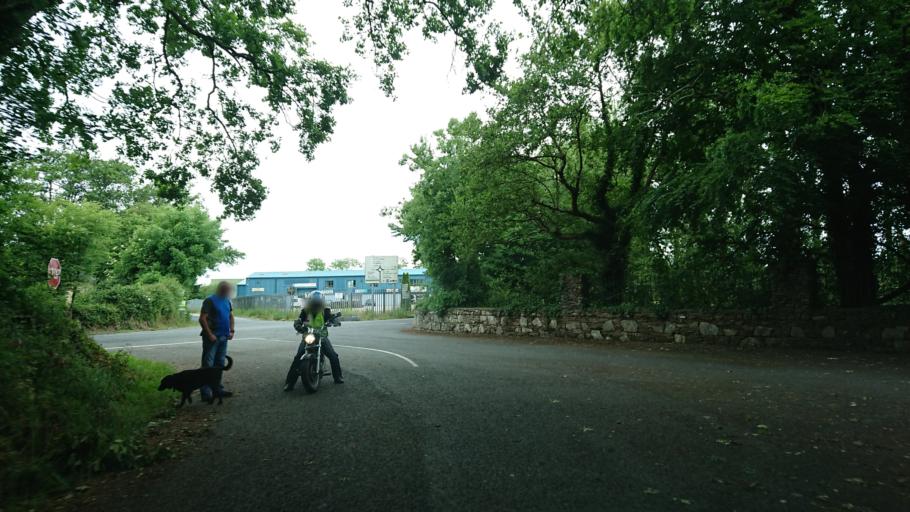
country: IE
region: Munster
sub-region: Waterford
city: Waterford
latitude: 52.2282
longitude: -7.1460
